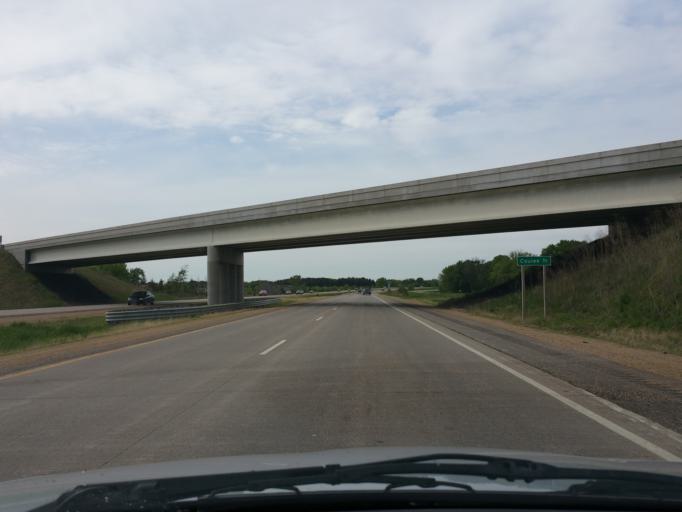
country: US
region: Minnesota
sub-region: Washington County
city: Lake Saint Croix Beach
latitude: 44.9307
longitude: -92.6843
